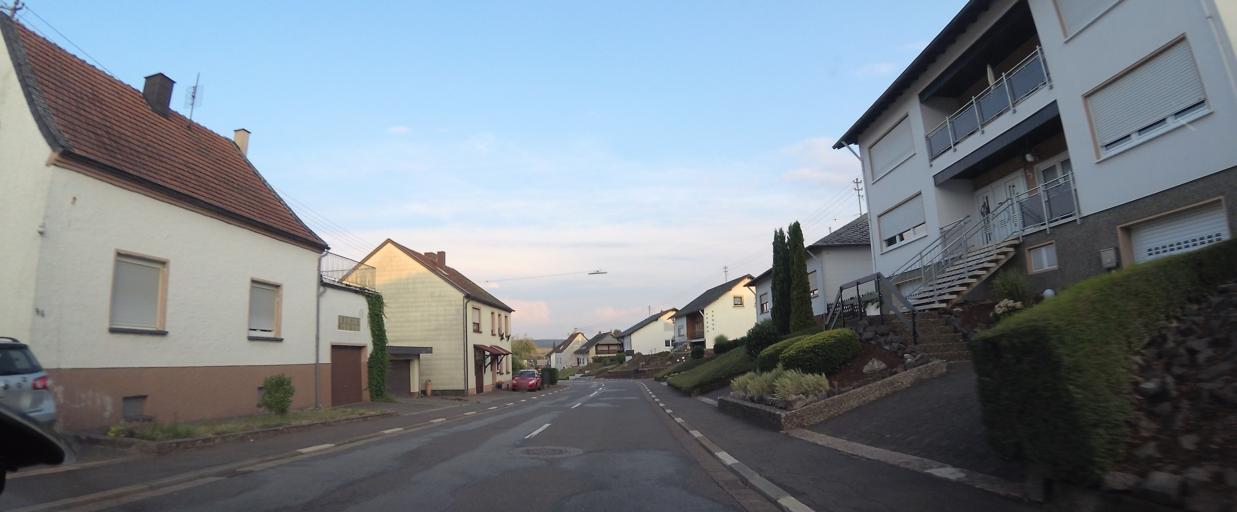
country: DE
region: Rheinland-Pfalz
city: Grimburg
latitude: 49.5849
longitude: 6.8812
